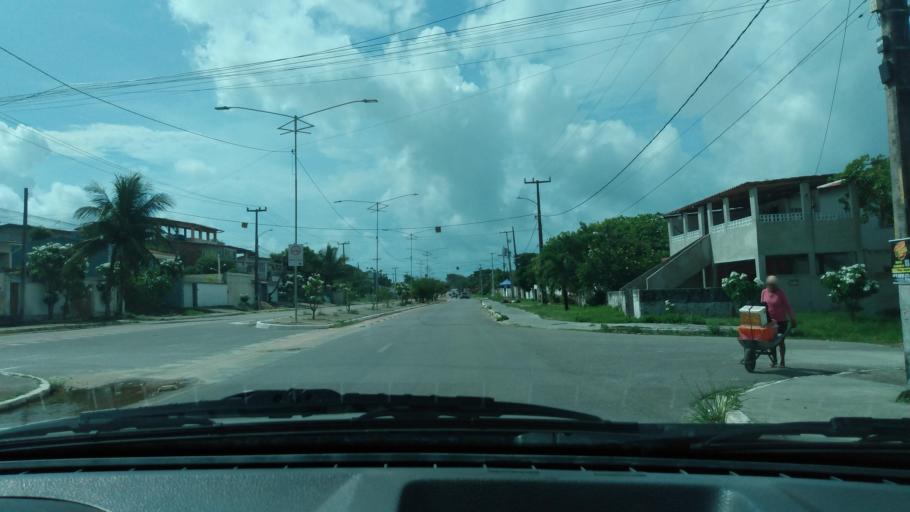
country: BR
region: Pernambuco
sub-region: Cabo De Santo Agostinho
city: Cabo
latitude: -8.3169
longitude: -34.9505
